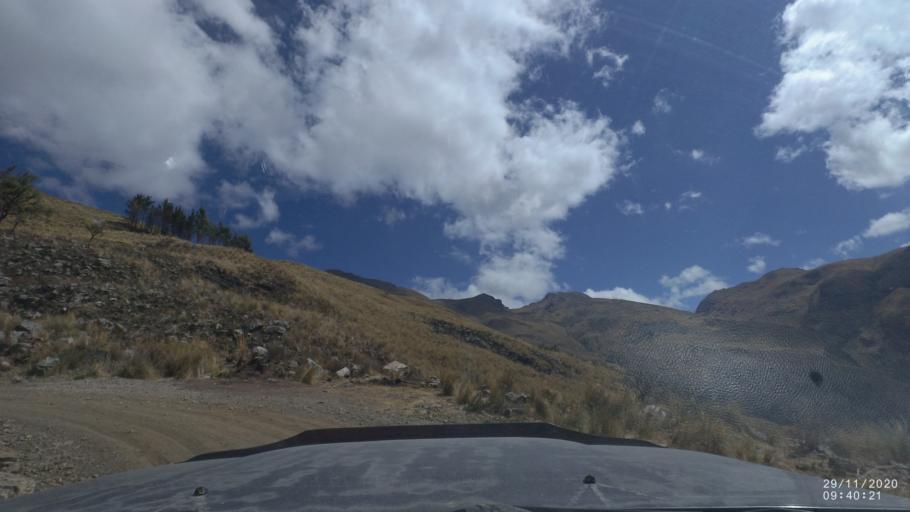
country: BO
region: Cochabamba
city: Cochabamba
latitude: -17.3029
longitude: -66.1798
